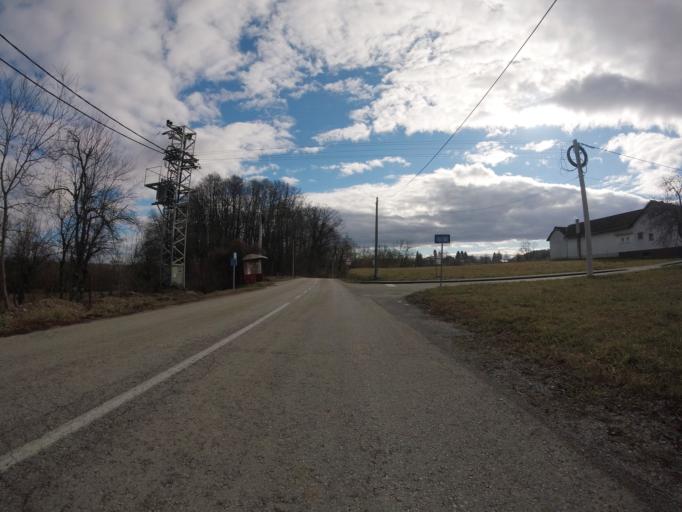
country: HR
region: Zagrebacka
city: Mraclin
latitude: 45.6369
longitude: 16.0593
